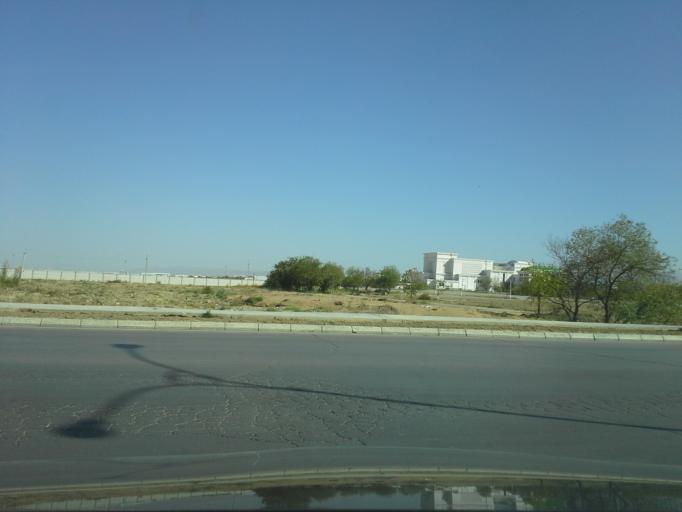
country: TM
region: Ahal
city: Ashgabat
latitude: 37.9939
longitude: 58.3229
